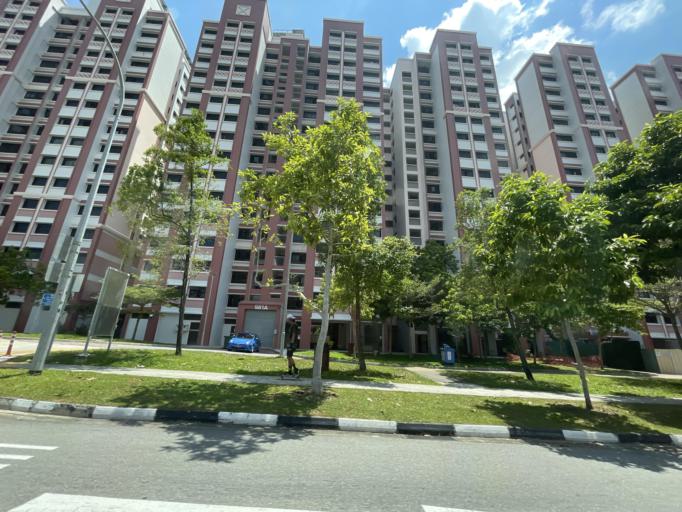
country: MY
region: Johor
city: Kampung Pasir Gudang Baru
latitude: 1.3808
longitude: 103.8806
